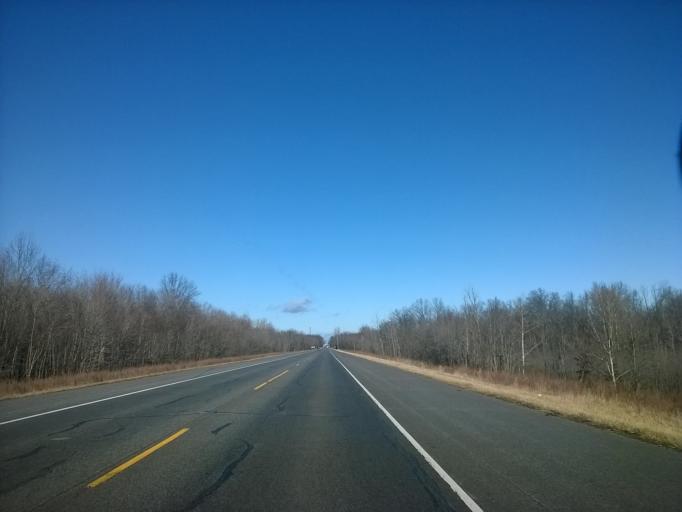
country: US
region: Indiana
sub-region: Scott County
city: Austin
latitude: 38.7653
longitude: -85.8188
